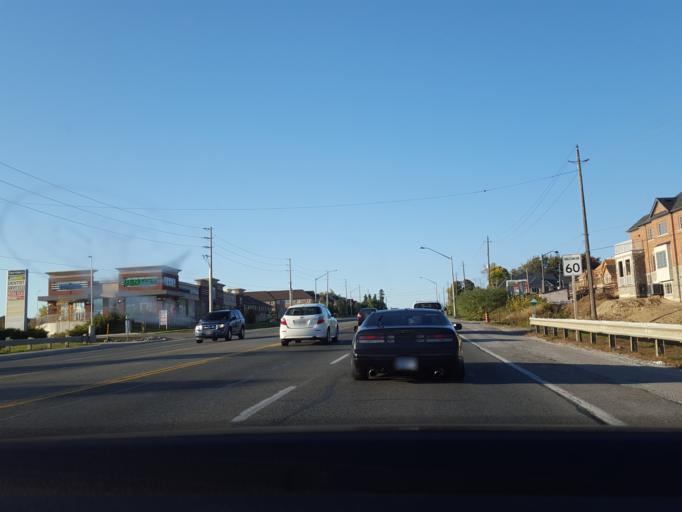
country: CA
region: Ontario
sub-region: York
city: Richmond Hill
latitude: 43.9149
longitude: -79.4474
